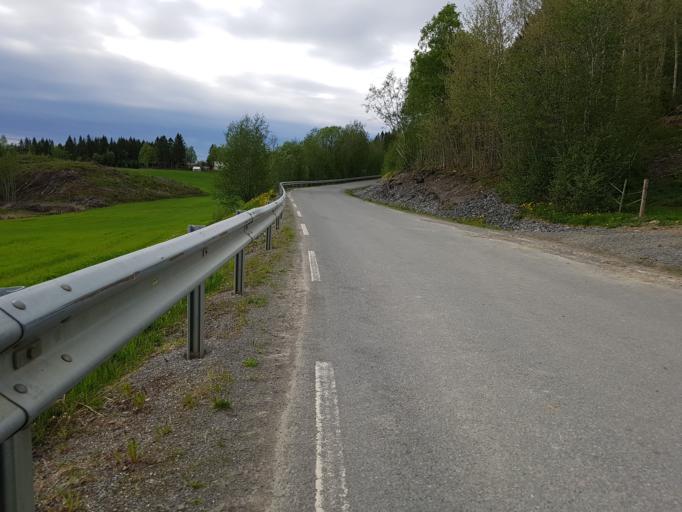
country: NO
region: Nord-Trondelag
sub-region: Levanger
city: Skogn
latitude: 63.6246
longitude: 11.2753
